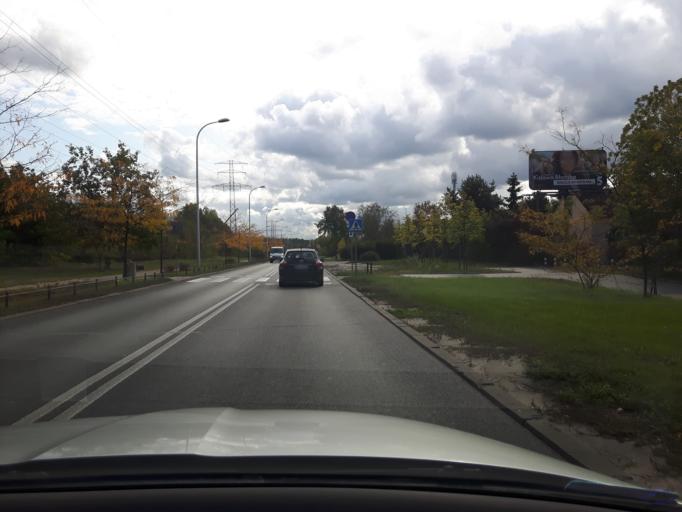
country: PL
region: Masovian Voivodeship
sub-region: Warszawa
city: Rembertow
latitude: 52.2404
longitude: 21.1406
